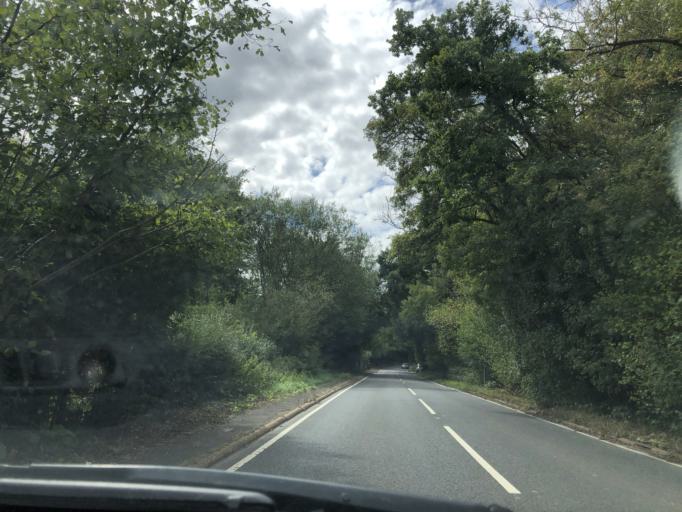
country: GB
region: England
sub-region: East Sussex
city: Forest Row
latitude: 51.0871
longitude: 0.0774
